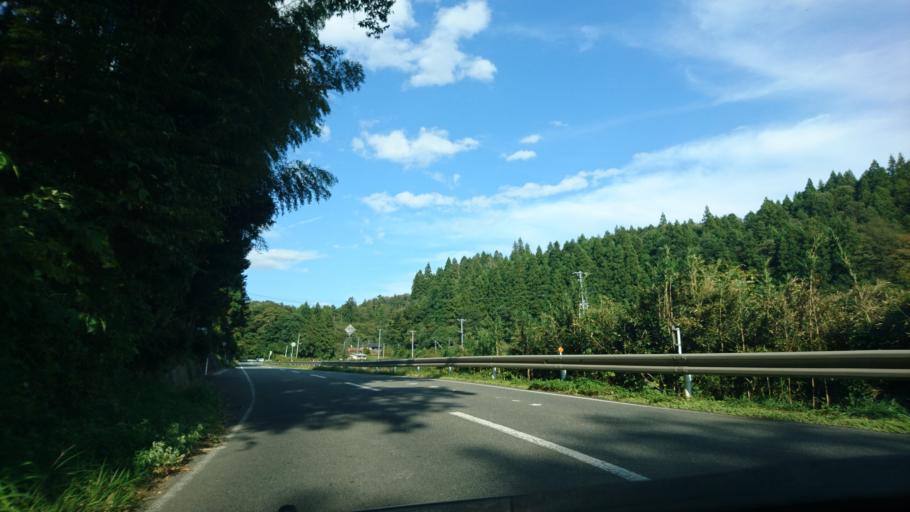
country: JP
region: Iwate
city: Ichinoseki
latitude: 38.8605
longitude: 141.3247
